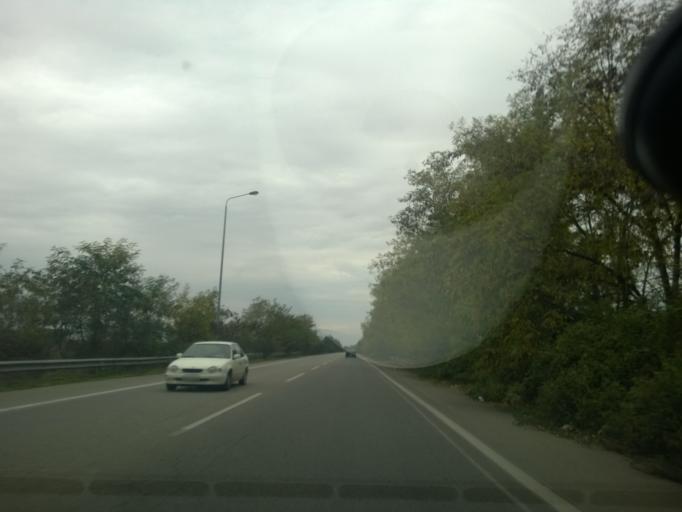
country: GR
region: Central Macedonia
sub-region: Nomos Pellis
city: Melissi
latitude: 40.7780
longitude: 22.3346
